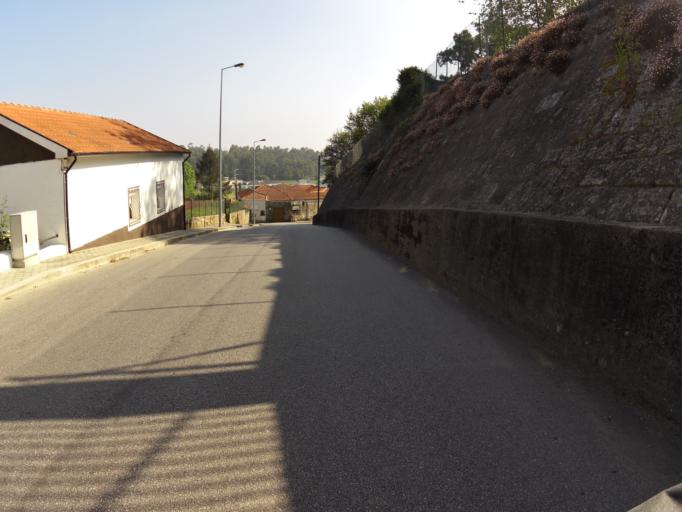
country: PT
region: Aveiro
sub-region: Santa Maria da Feira
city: Argoncilhe
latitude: 41.0340
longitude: -8.5499
